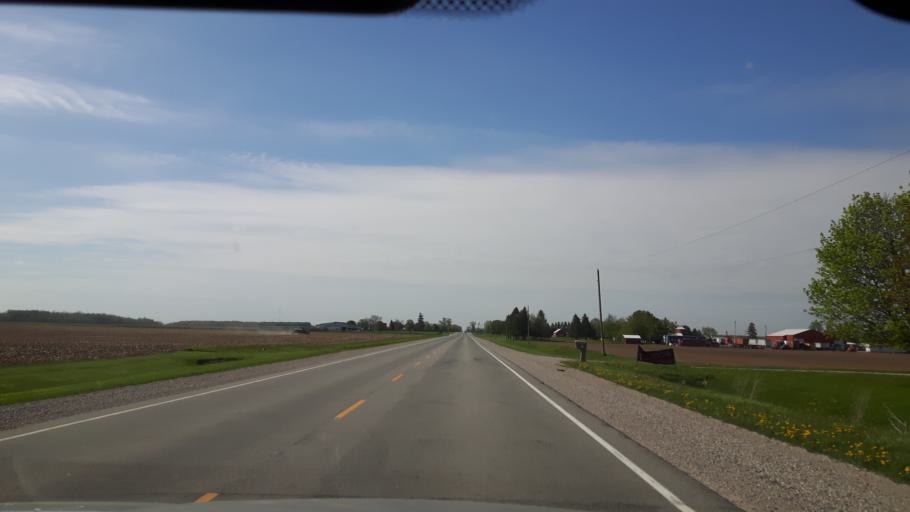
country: CA
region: Ontario
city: Bluewater
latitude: 43.4569
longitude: -81.5032
